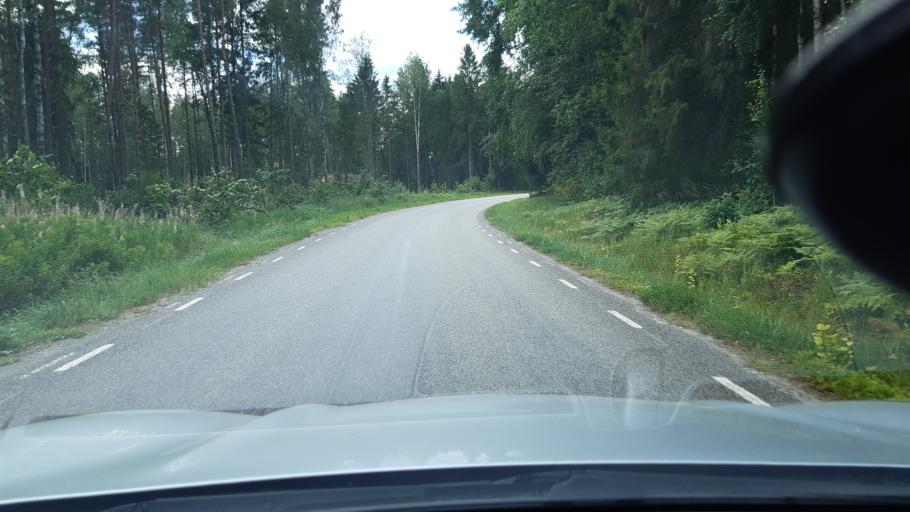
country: EE
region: Raplamaa
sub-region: Jaervakandi vald
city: Jarvakandi
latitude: 58.7897
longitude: 24.8269
